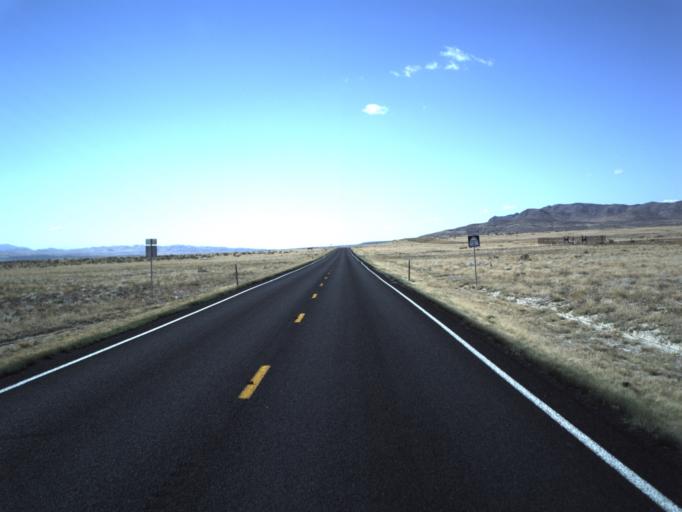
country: US
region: Utah
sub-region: Millard County
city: Fillmore
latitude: 38.9154
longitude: -112.8142
